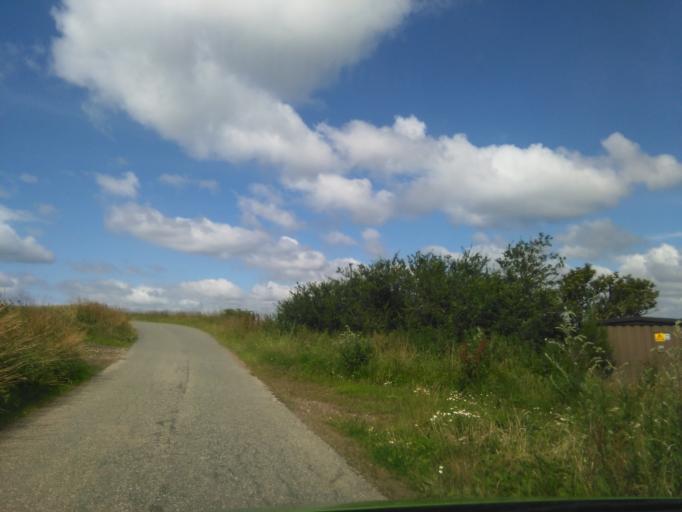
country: DK
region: Central Jutland
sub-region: Syddjurs Kommune
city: Ronde
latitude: 56.2394
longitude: 10.4797
